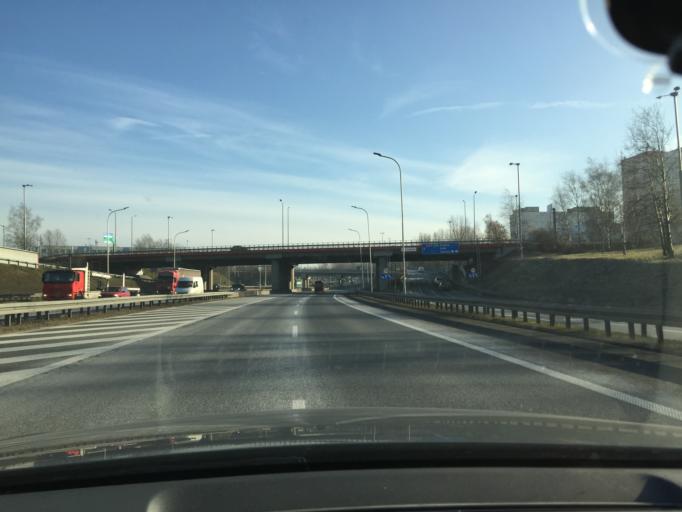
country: PL
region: Silesian Voivodeship
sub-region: Katowice
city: Katowice
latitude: 50.2503
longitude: 18.9983
